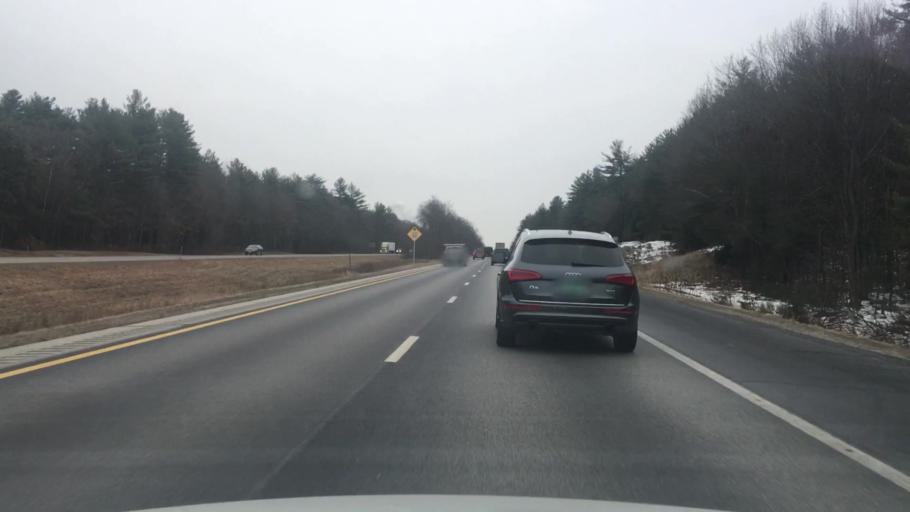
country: US
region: New Hampshire
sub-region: Merrimack County
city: Concord
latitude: 43.1760
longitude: -71.5594
